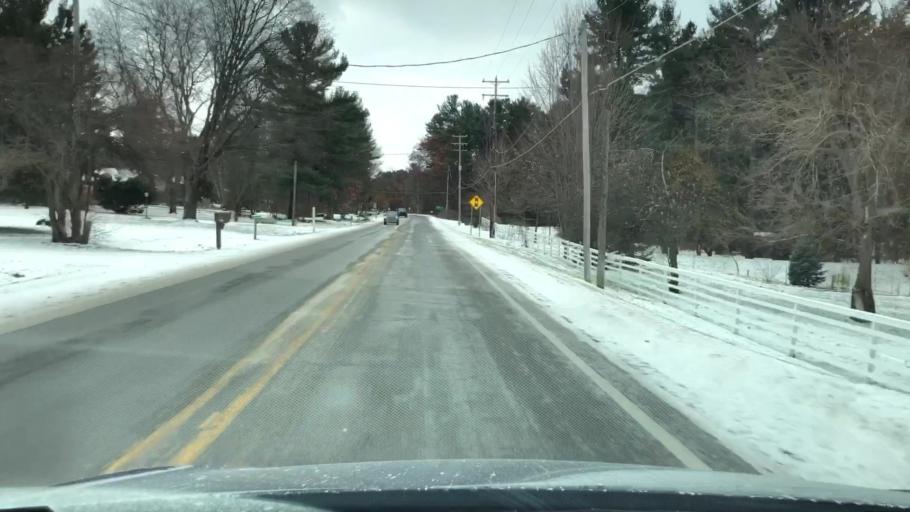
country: US
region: Michigan
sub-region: Grand Traverse County
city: Traverse City
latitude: 44.7762
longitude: -85.5910
